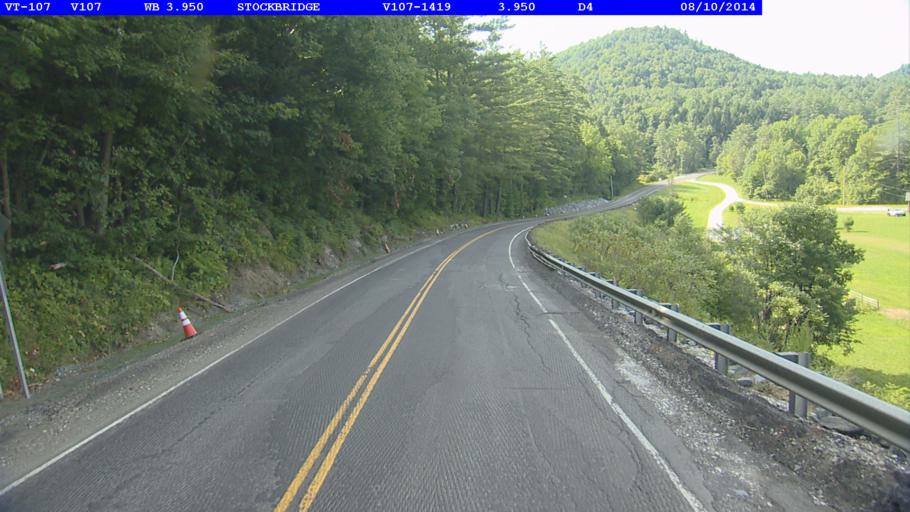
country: US
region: Vermont
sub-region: Orange County
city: Randolph
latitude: 43.7734
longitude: -72.7038
